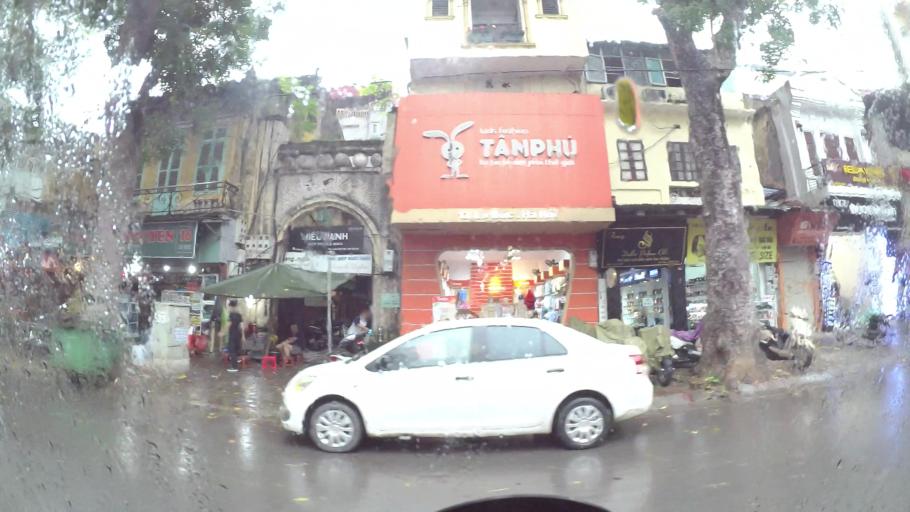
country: VN
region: Ha Noi
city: Hai BaTrung
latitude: 21.0177
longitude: 105.8554
